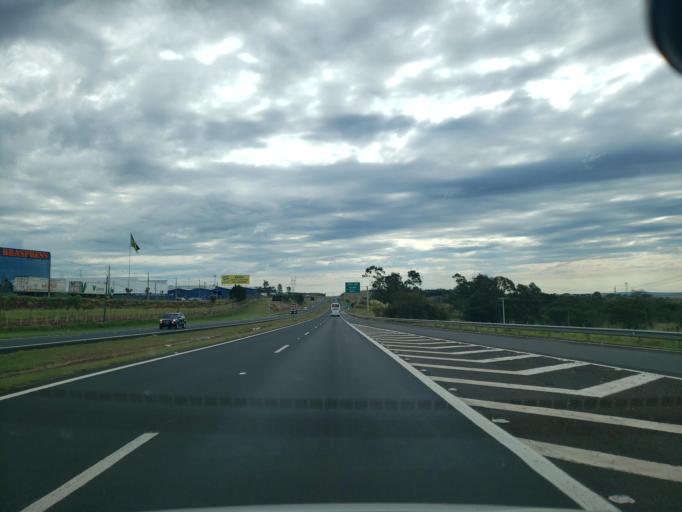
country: BR
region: Sao Paulo
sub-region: Bauru
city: Bauru
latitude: -22.2794
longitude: -49.0892
